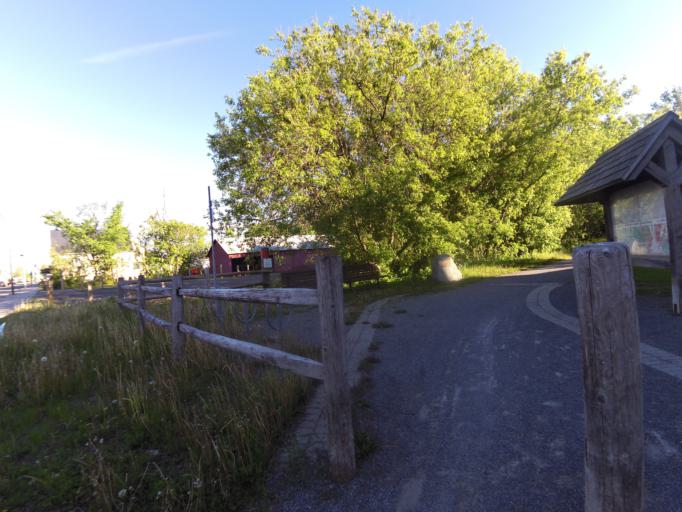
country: CA
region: Ontario
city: Bells Corners
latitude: 45.2582
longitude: -75.9208
